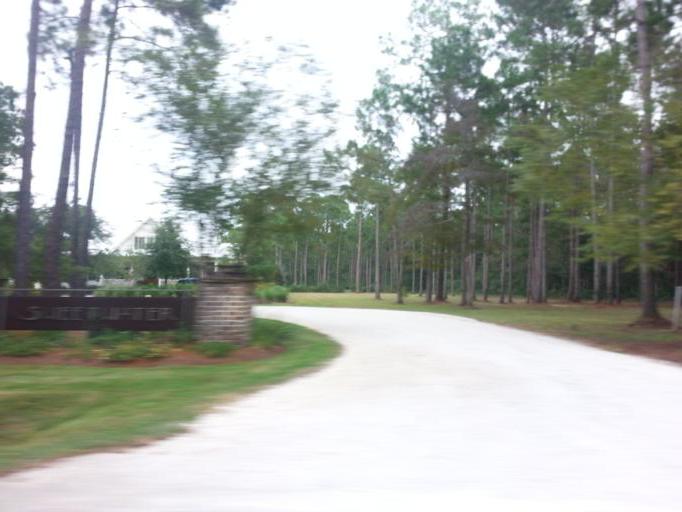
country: US
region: Alabama
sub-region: Baldwin County
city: Point Clear
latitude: 30.5016
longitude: -87.9224
